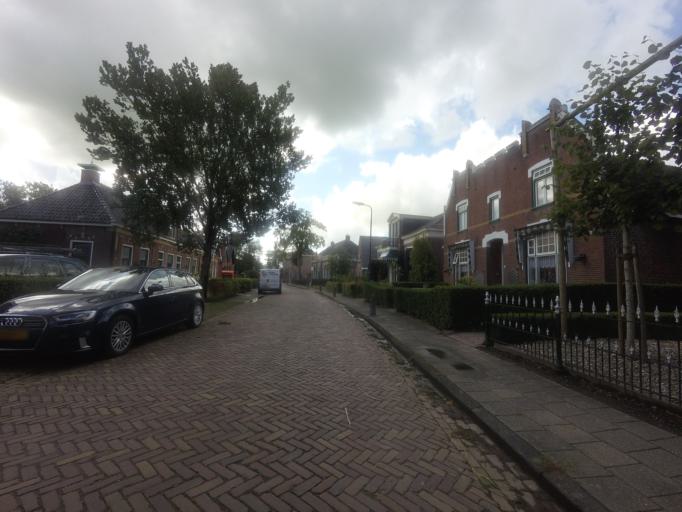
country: NL
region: Friesland
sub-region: Gemeente Littenseradiel
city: Makkum
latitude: 53.0882
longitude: 5.6961
